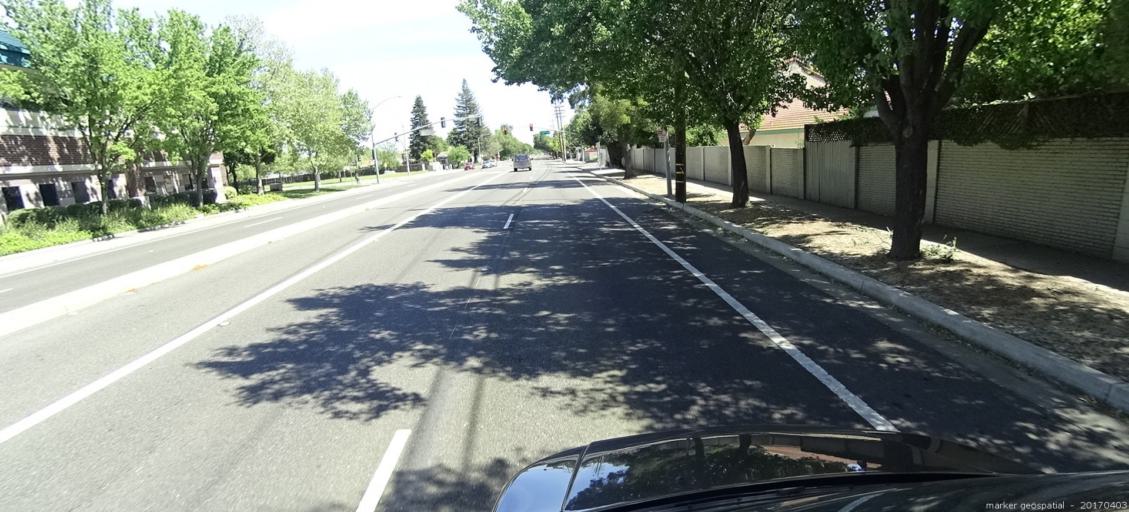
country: US
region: California
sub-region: Sacramento County
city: Sacramento
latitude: 38.6274
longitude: -121.4949
